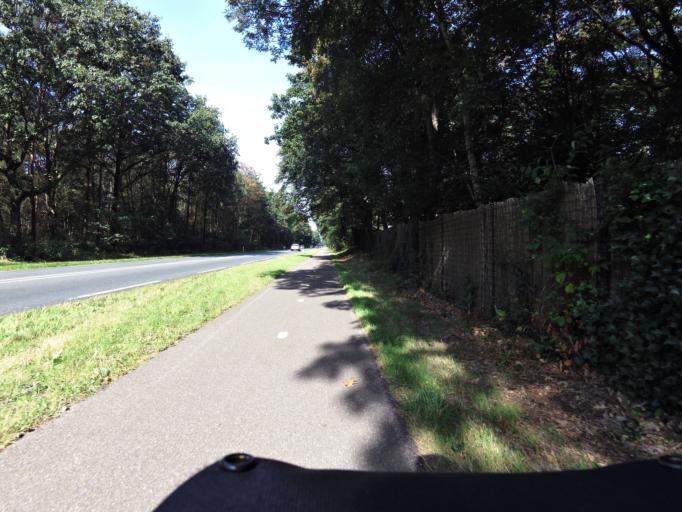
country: NL
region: Gelderland
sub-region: Gemeente Apeldoorn
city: Uddel
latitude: 52.2261
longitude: 5.7762
